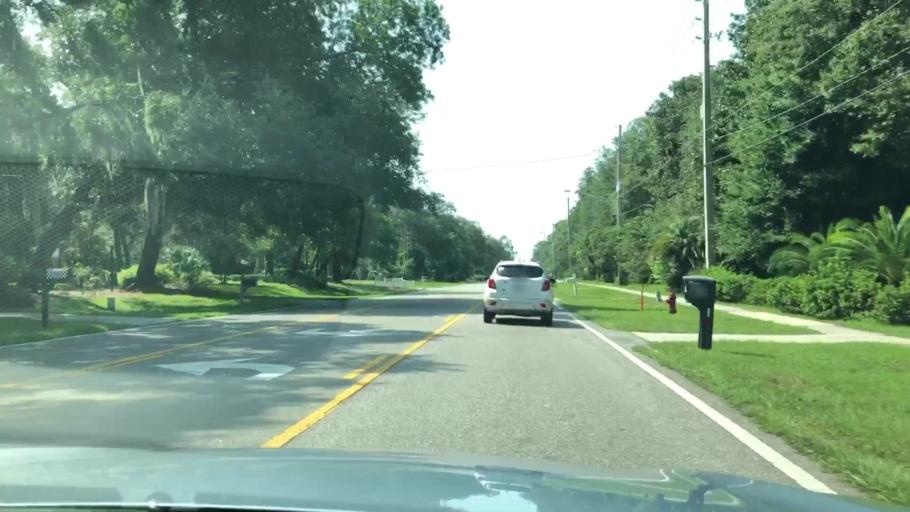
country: US
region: Florida
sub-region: Duval County
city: Neptune Beach
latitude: 30.3180
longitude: -81.4082
